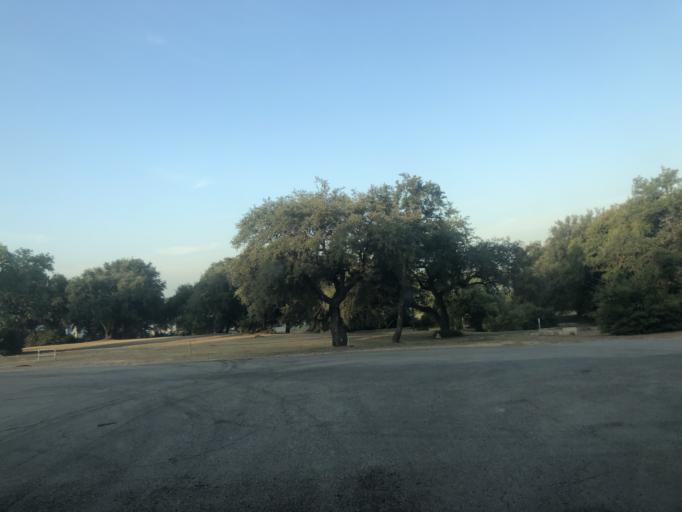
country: US
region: Texas
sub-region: Tarrant County
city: Lake Worth
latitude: 32.7962
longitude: -97.4525
